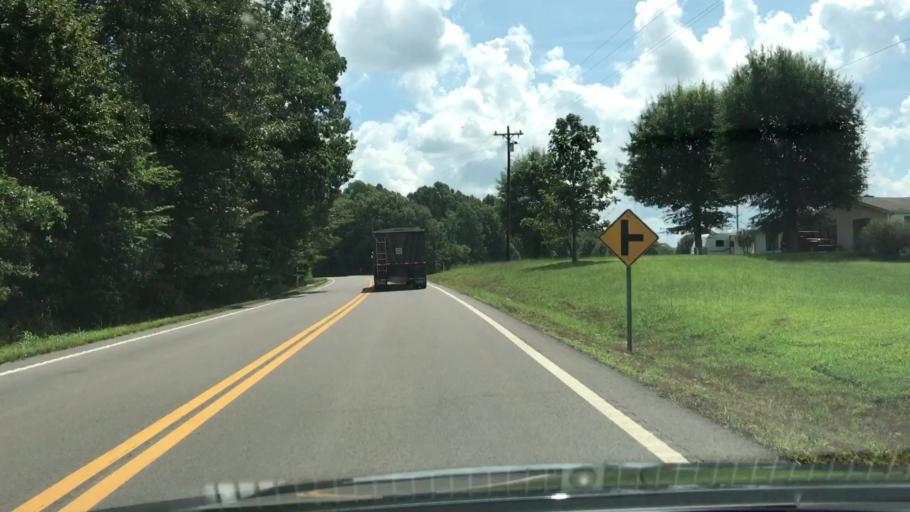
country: US
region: Tennessee
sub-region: Robertson County
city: Springfield
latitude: 36.6266
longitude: -86.9531
